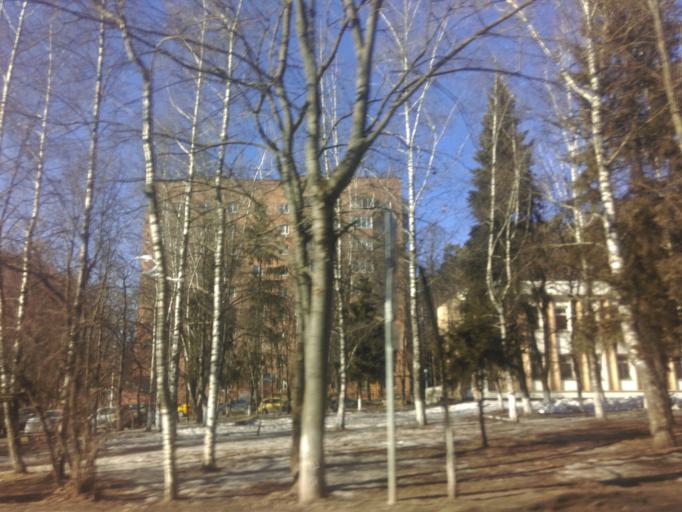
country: RU
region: Moskovskaya
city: Kommunarka
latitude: 55.5320
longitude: 37.4488
